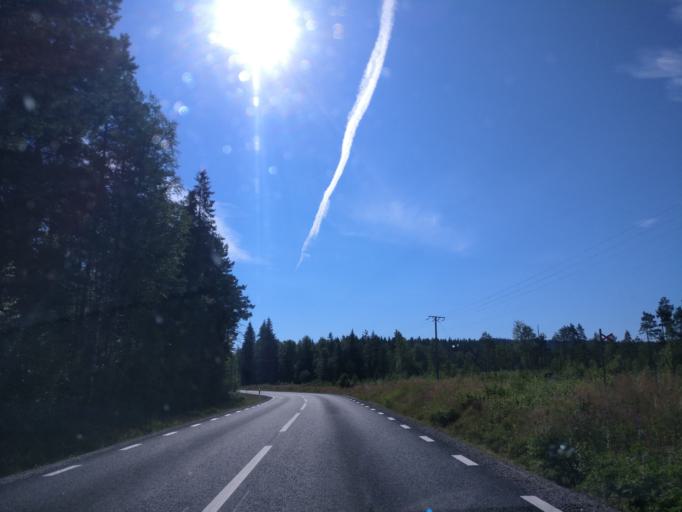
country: SE
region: Vaermland
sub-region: Hagfors Kommun
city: Hagfors
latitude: 60.0349
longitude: 13.8332
